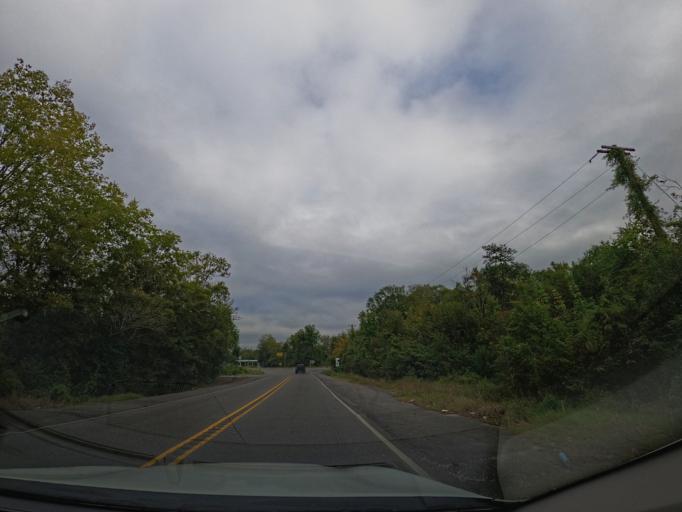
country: US
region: Louisiana
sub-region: Saint Mary Parish
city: Amelia
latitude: 29.6851
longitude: -90.9988
